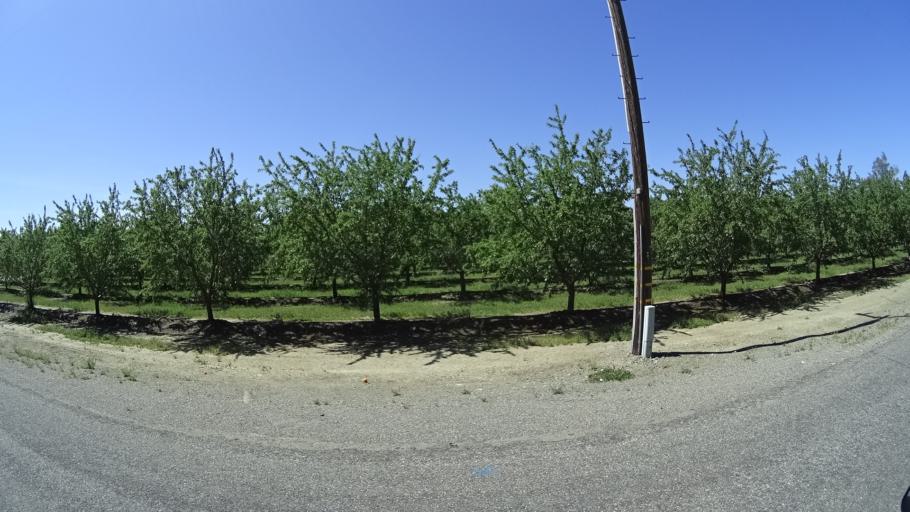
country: US
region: California
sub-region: Glenn County
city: Orland
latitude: 39.7367
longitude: -122.1594
